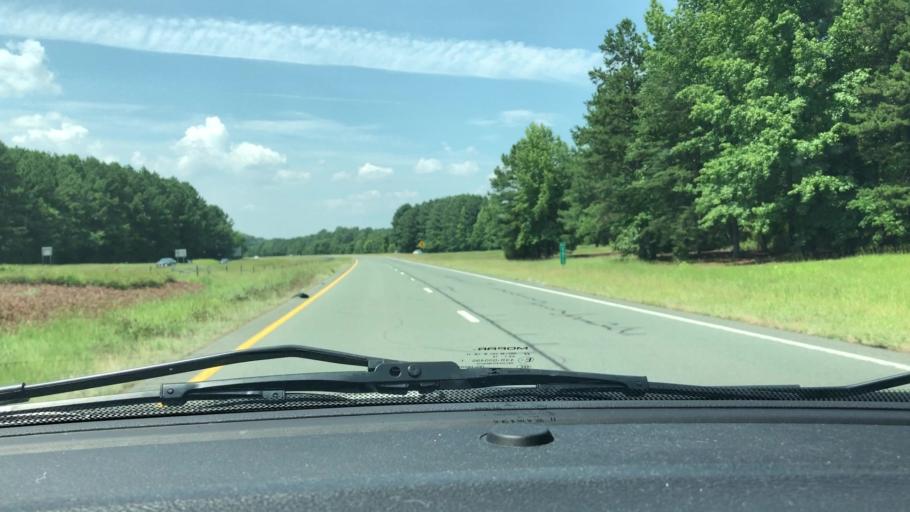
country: US
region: North Carolina
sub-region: Chatham County
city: Siler City
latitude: 35.7350
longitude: -79.4320
